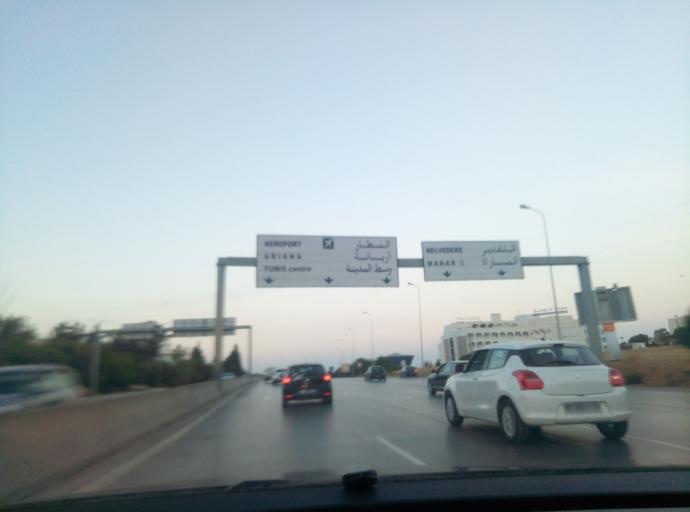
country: TN
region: Tunis
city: Tunis
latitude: 36.8311
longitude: 10.1525
